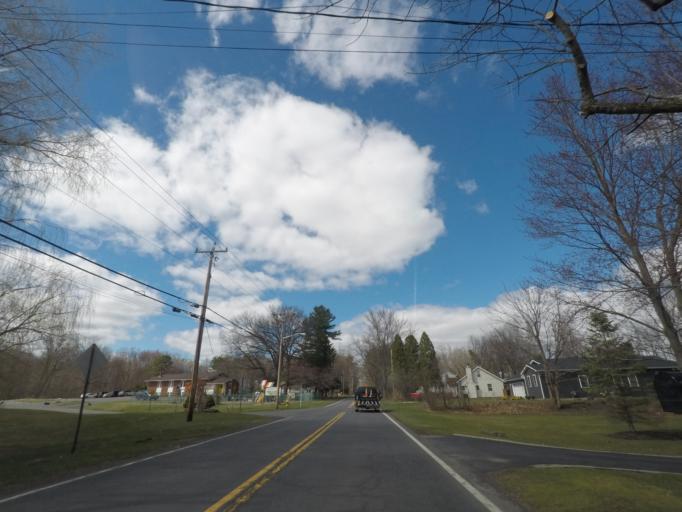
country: US
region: New York
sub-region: Albany County
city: Delmar
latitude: 42.5825
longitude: -73.8298
